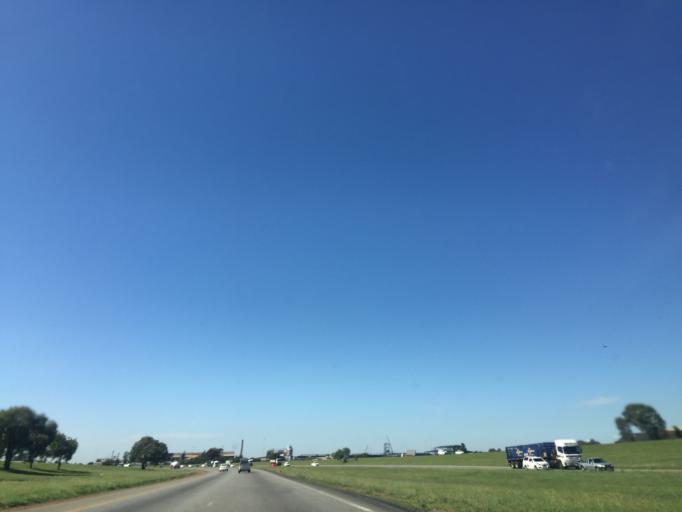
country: ZA
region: Gauteng
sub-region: Sedibeng District Municipality
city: Meyerton
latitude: -26.5614
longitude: 27.9992
